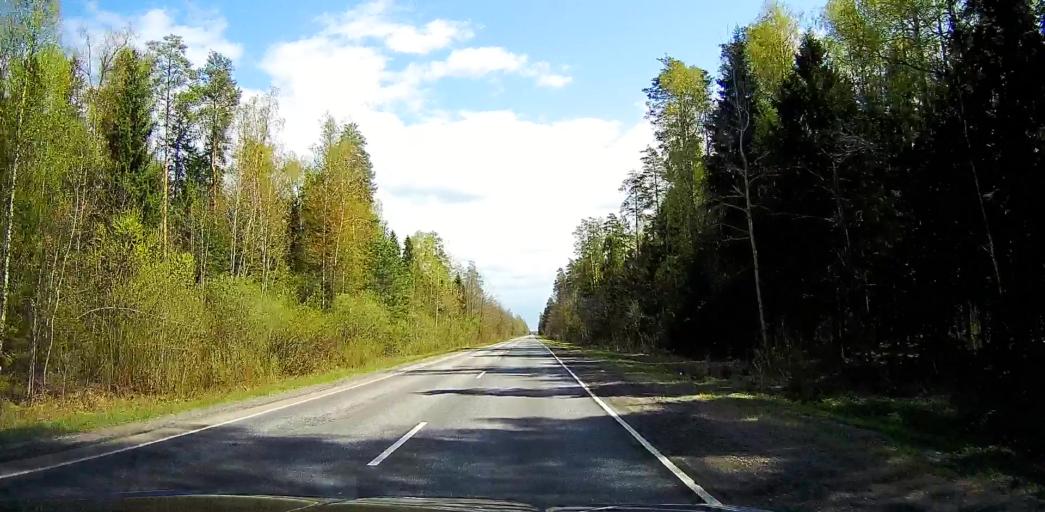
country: RU
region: Moskovskaya
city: Davydovo
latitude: 55.5515
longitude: 38.7662
